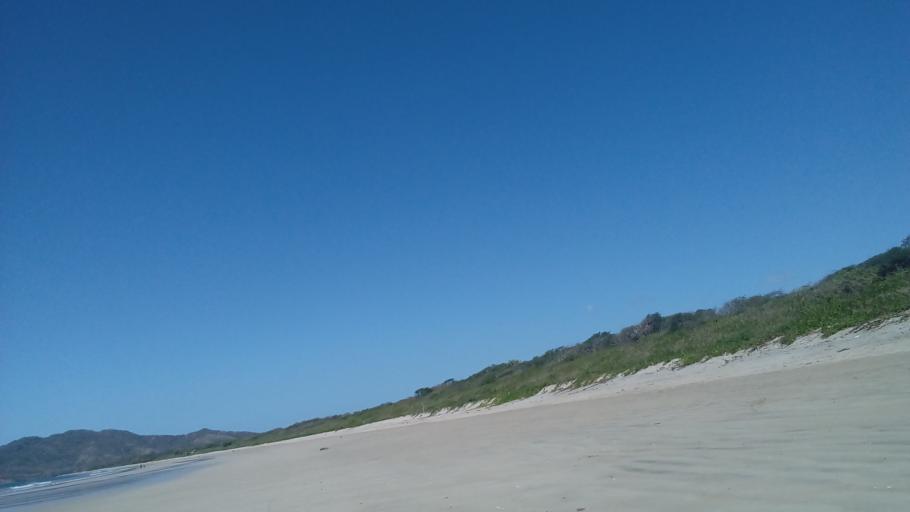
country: CR
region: Guanacaste
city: Santa Cruz
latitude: 10.3223
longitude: -85.8413
